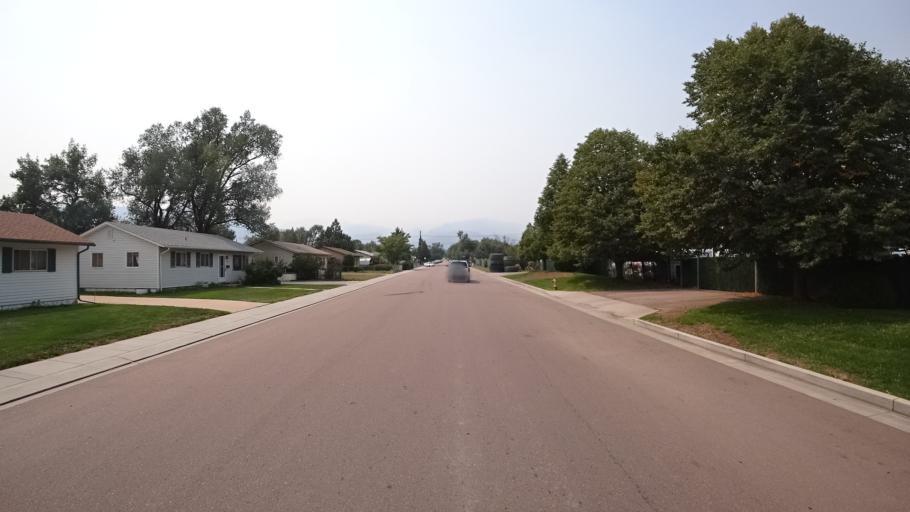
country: US
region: Colorado
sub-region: El Paso County
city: Stratmoor
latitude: 38.7997
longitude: -104.8020
